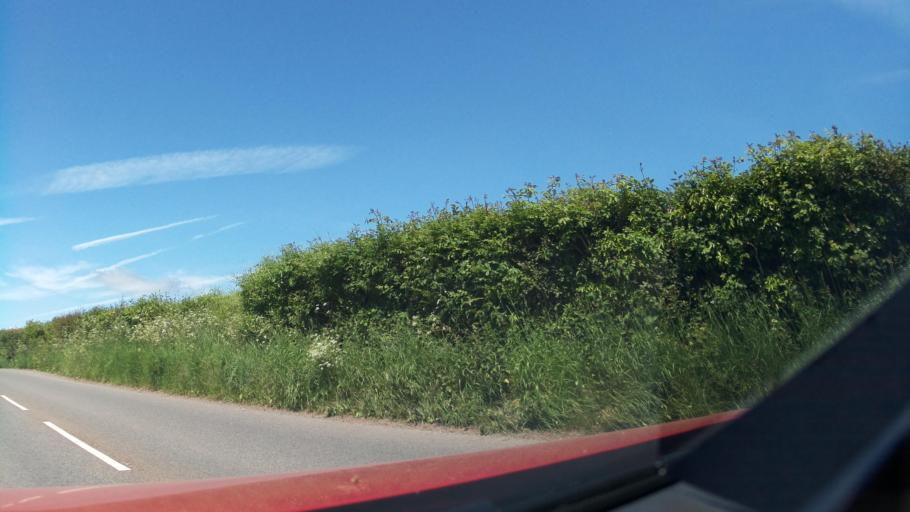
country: GB
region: Wales
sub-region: Monmouthshire
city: Caldicot
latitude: 51.6366
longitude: -2.7495
